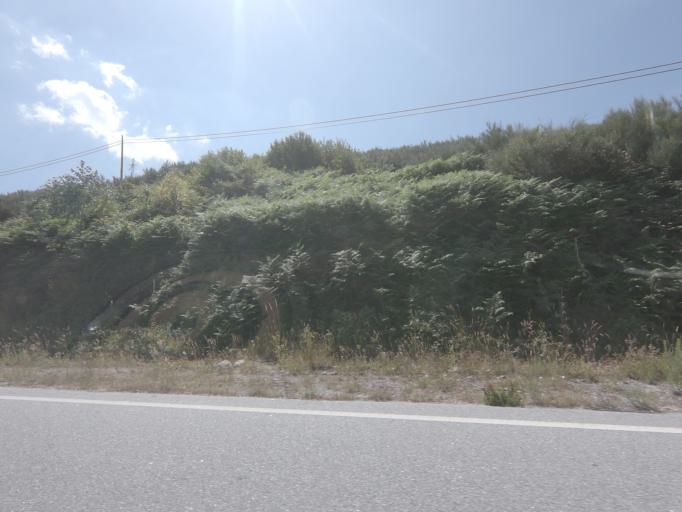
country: PT
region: Viseu
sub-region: Tarouca
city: Tarouca
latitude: 40.9915
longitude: -7.7802
